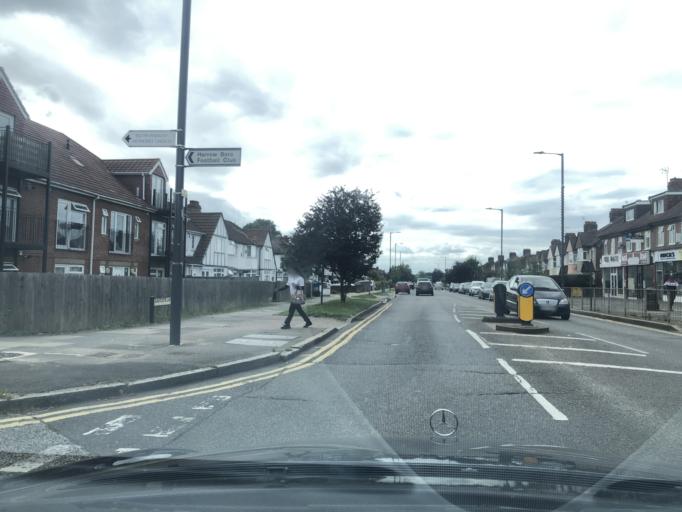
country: GB
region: England
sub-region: Greater London
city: Northolt
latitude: 51.5618
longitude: -0.3726
